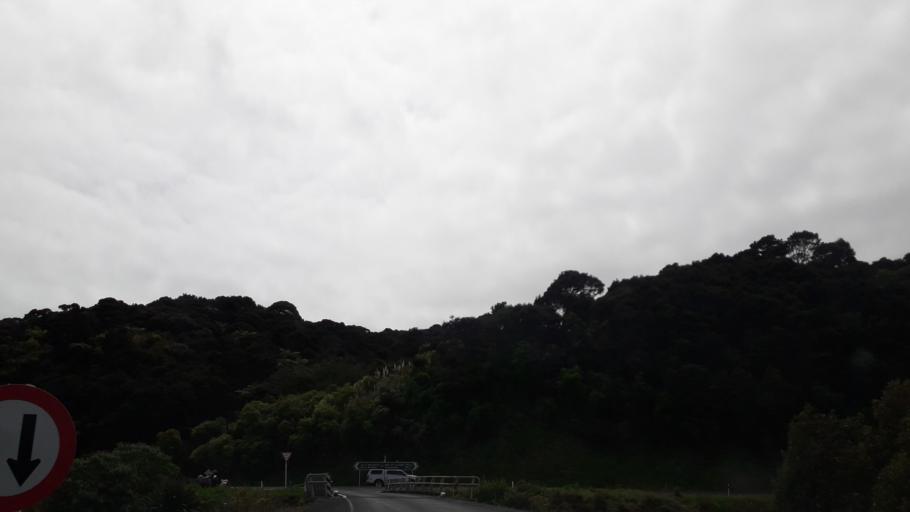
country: NZ
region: Northland
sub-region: Far North District
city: Taipa
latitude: -35.0119
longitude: 173.5499
